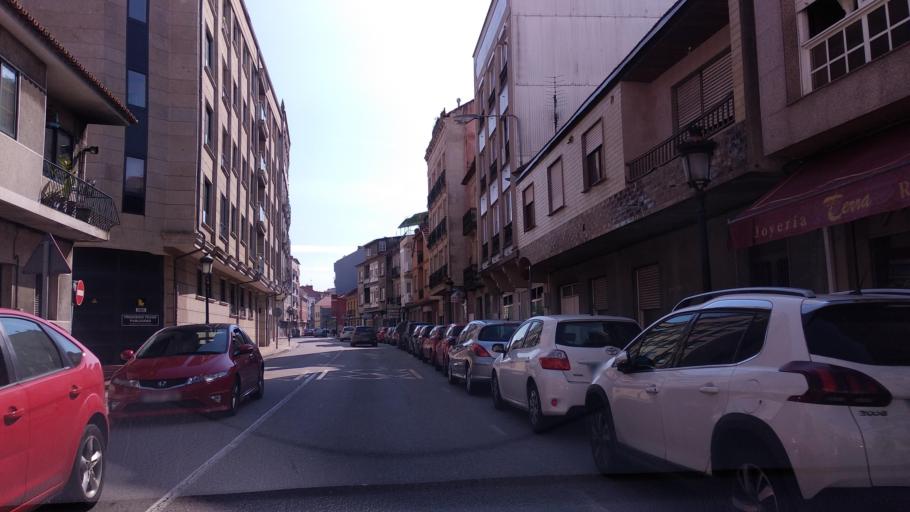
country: ES
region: Galicia
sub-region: Provincia de Pontevedra
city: Moana
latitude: 42.2841
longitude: -8.7352
